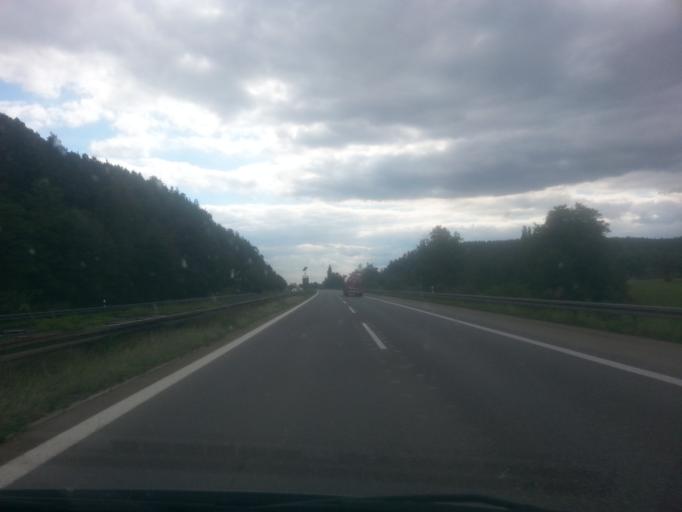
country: DE
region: Bavaria
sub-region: Upper Palatinate
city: Nabburg
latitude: 49.4269
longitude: 12.1726
